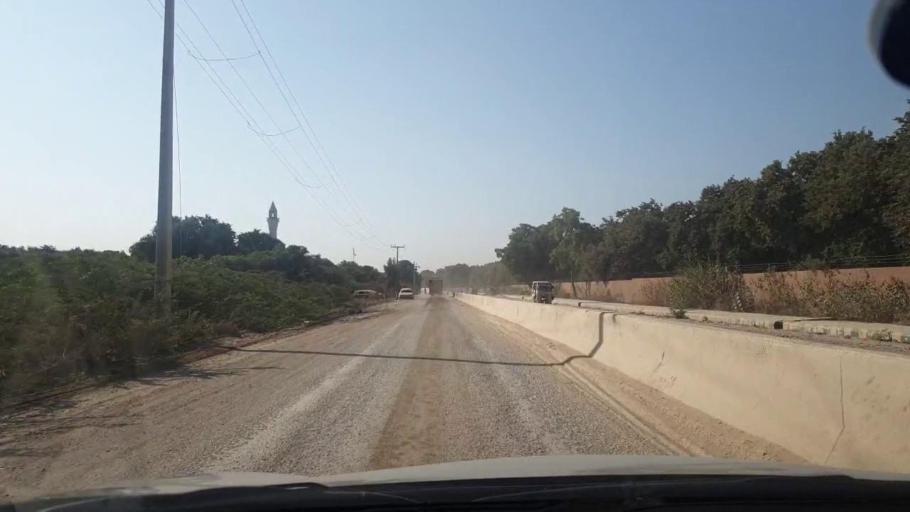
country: PK
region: Sindh
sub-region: Karachi District
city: Karachi
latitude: 25.0893
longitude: 67.0130
